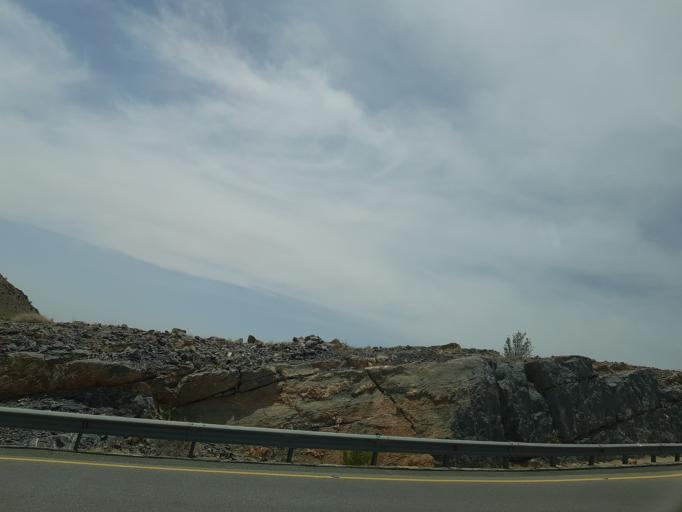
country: OM
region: Muhafazat ad Dakhiliyah
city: Izki
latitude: 22.9970
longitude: 57.7057
